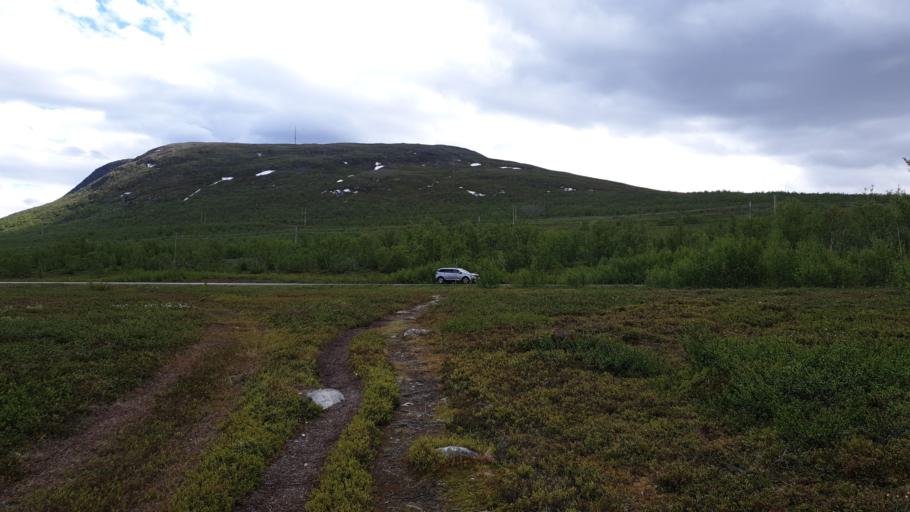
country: SE
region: Norrbotten
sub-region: Kiruna Kommun
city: Kiruna
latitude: 68.2326
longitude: 19.6199
